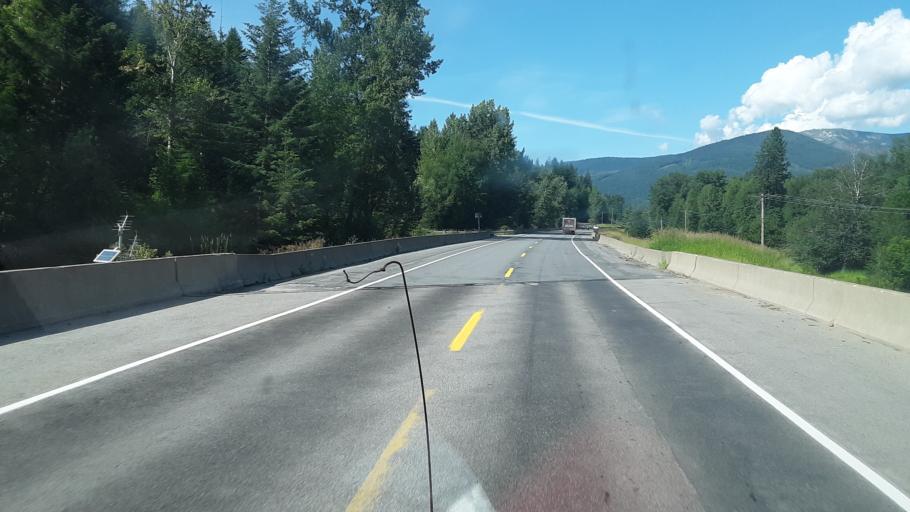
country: US
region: Idaho
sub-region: Bonner County
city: Ponderay
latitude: 48.4200
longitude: -116.5019
